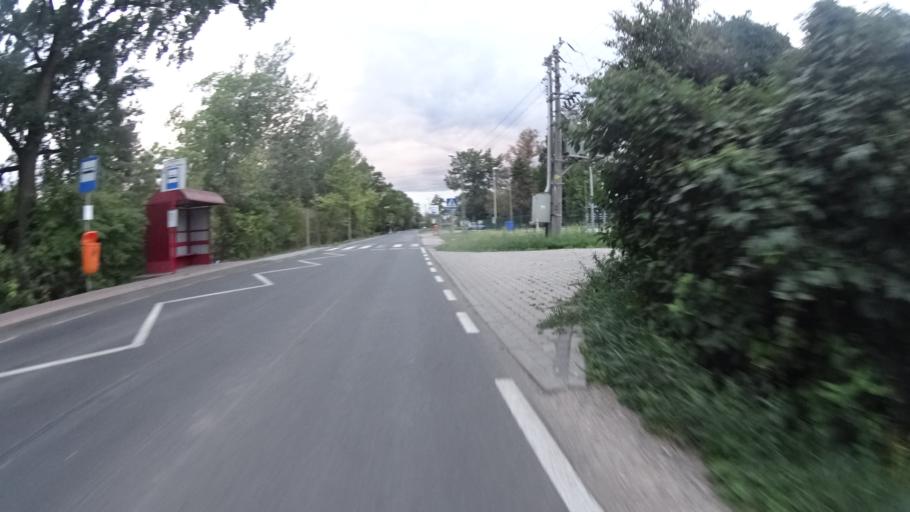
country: PL
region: Masovian Voivodeship
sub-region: Powiat warszawski zachodni
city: Ozarow Mazowiecki
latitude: 52.2314
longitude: 20.7649
